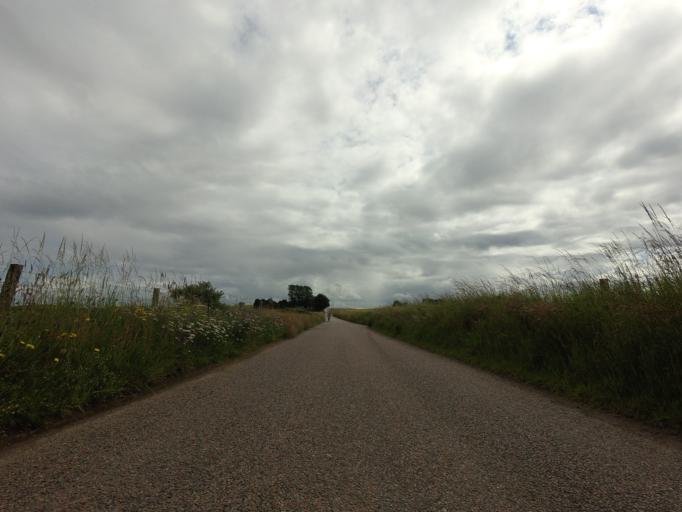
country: GB
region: Scotland
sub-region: Moray
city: Fochabers
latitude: 57.6672
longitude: -3.1526
